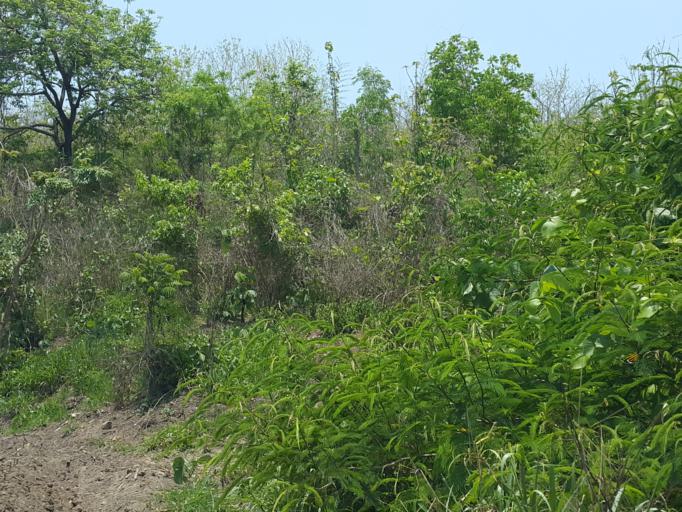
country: TH
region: Kanchanaburi
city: Sai Yok
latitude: 14.2400
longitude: 98.8736
